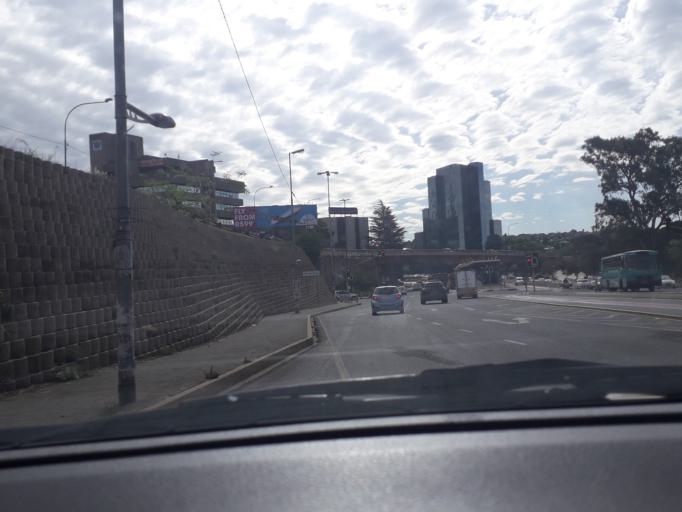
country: ZA
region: Gauteng
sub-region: City of Johannesburg Metropolitan Municipality
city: Johannesburg
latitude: -26.1837
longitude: 28.0218
